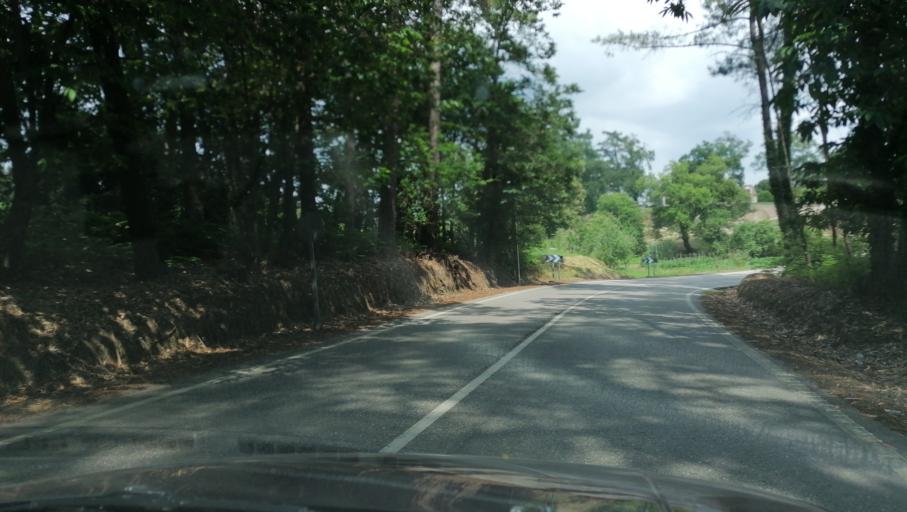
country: ES
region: Galicia
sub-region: Provincia de Pontevedra
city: Tomino
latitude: 42.0148
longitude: -8.7053
